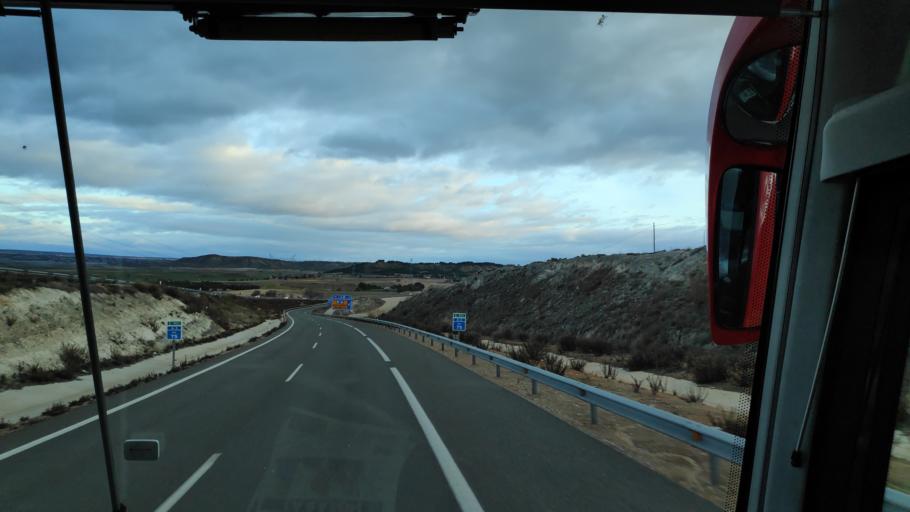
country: ES
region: Castille-La Mancha
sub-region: Provincia de Cuenca
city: Belinchon
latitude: 40.0436
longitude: -3.0593
